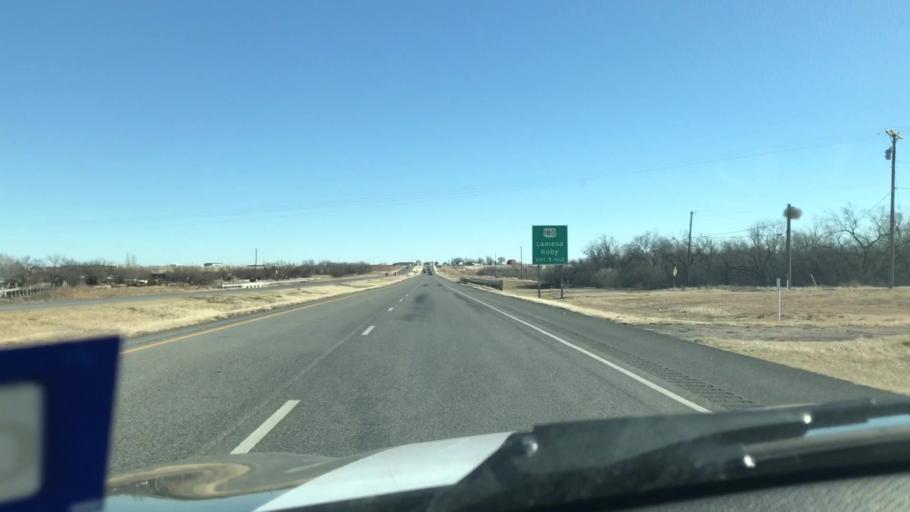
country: US
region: Texas
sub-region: Scurry County
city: Snyder
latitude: 32.7194
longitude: -100.8827
